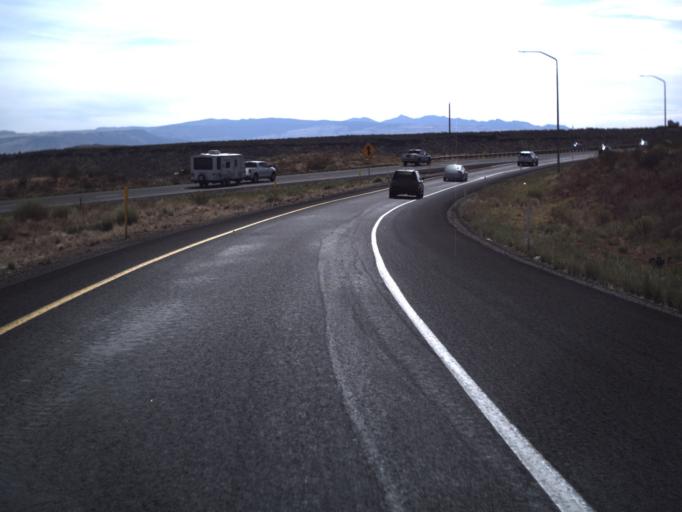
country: US
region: Utah
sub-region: Washington County
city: Washington
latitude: 37.1656
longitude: -113.4560
